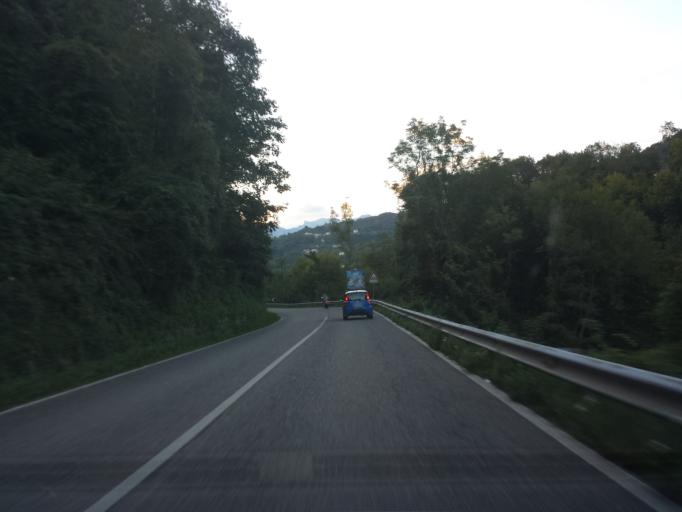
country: IT
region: Veneto
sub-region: Provincia di Vicenza
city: San Quirico
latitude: 45.6916
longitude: 11.2595
